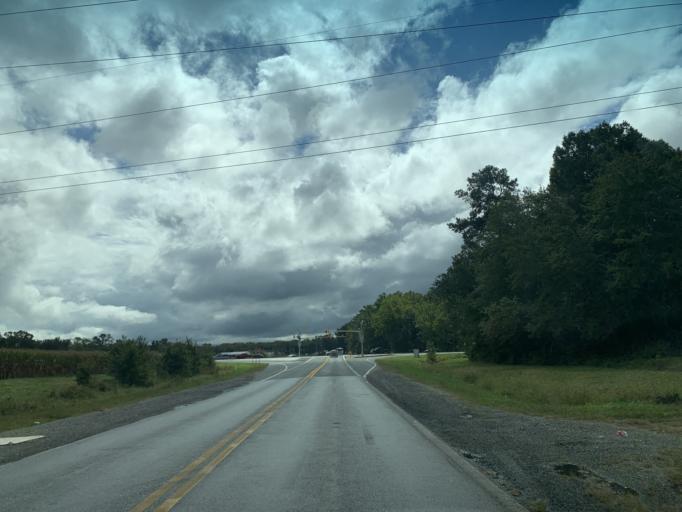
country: US
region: Maryland
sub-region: Caroline County
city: Denton
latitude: 38.8979
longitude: -75.8374
